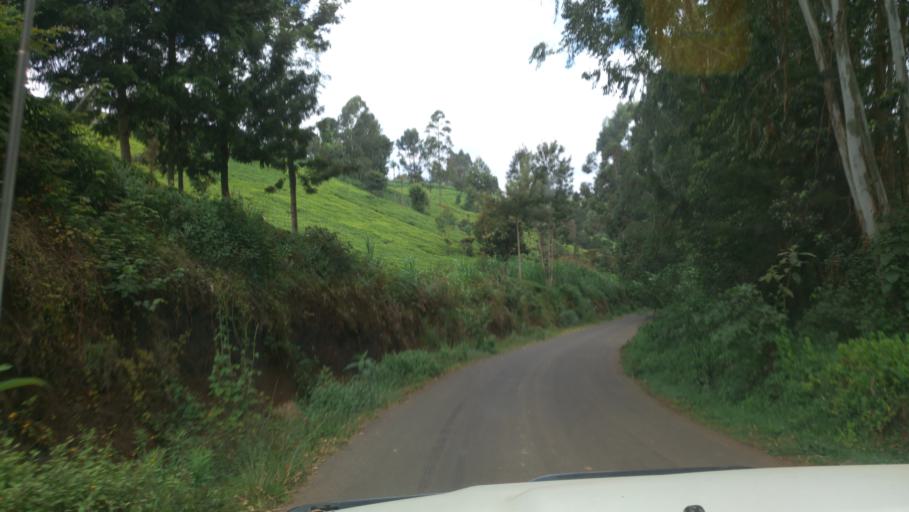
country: KE
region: Murang'a District
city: Kangema
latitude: -0.7691
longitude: 36.8370
